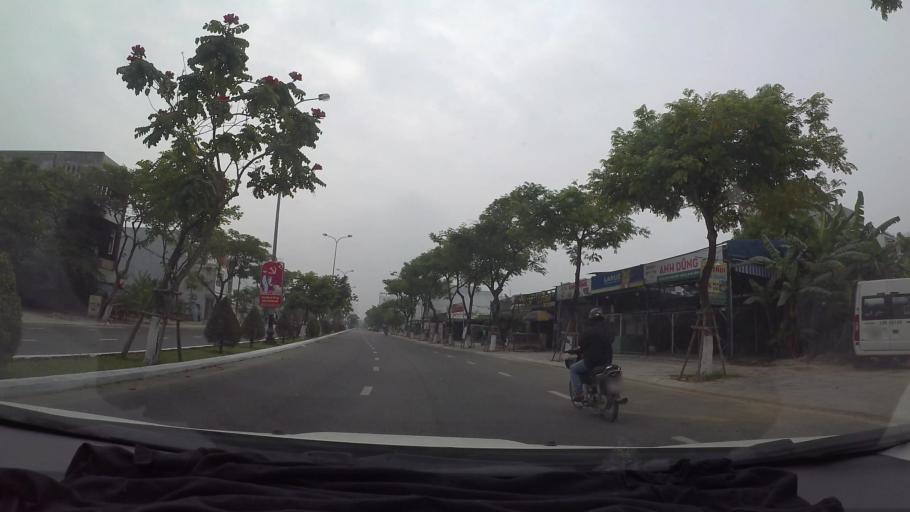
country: VN
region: Da Nang
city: Cam Le
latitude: 16.0301
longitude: 108.2123
